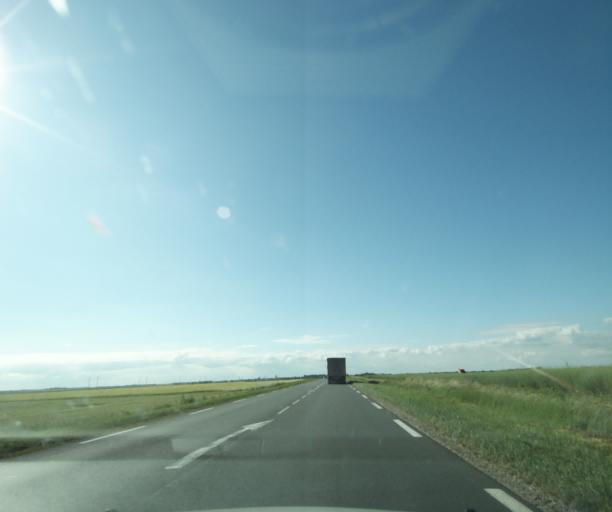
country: FR
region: Centre
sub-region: Departement d'Eure-et-Loir
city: Janville
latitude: 48.2470
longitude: 1.7728
